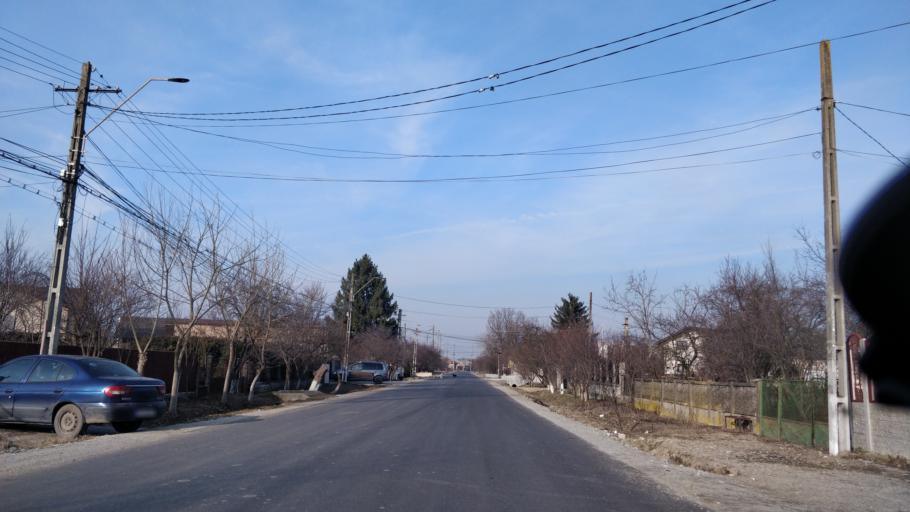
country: RO
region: Giurgiu
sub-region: Comuna Ulmi
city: Trestieni
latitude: 44.5095
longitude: 25.7636
